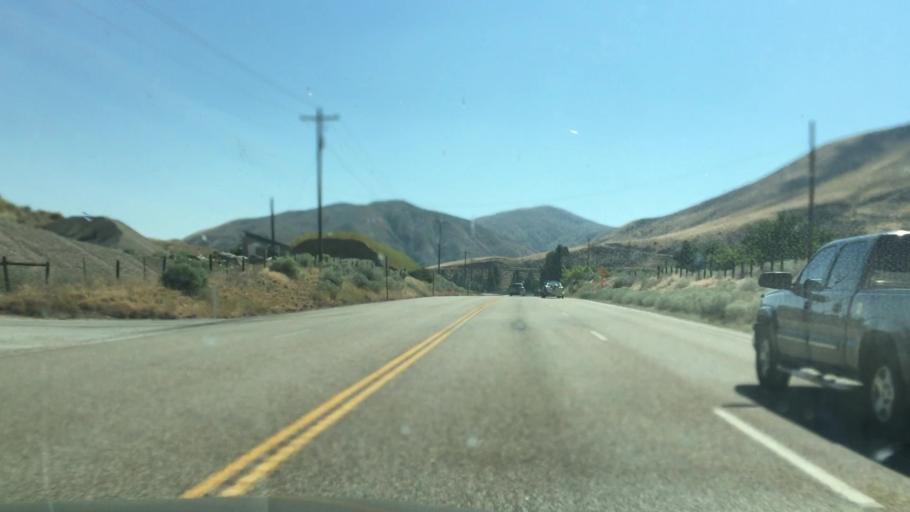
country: US
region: Idaho
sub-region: Gem County
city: Emmett
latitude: 43.9979
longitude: -116.1837
